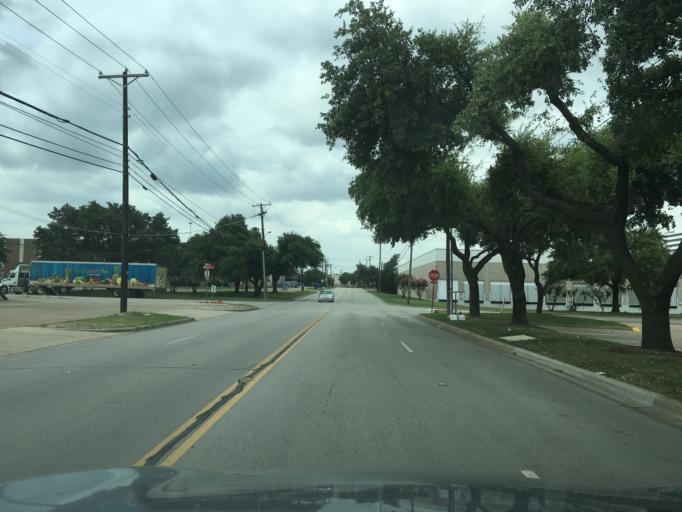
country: US
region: Texas
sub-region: Dallas County
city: Addison
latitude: 32.9311
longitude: -96.8305
